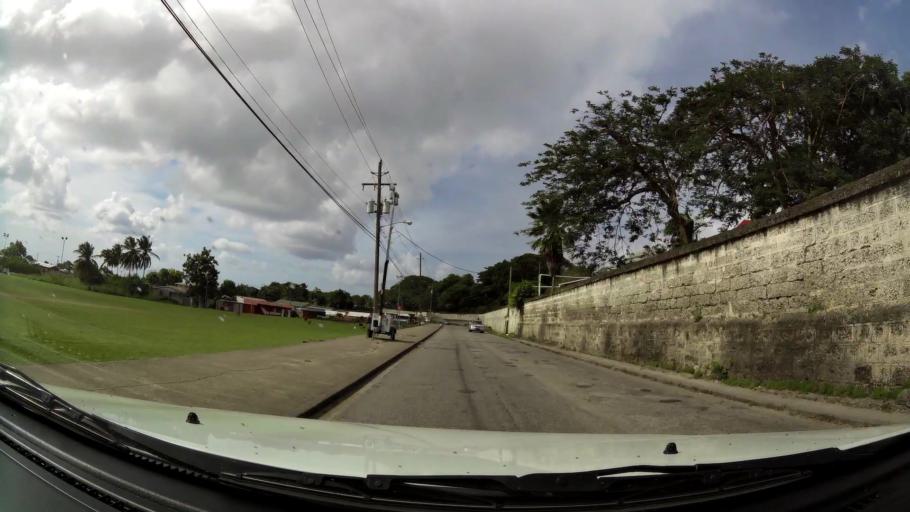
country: BB
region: Saint Michael
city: Bridgetown
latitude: 13.1232
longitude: -59.6045
